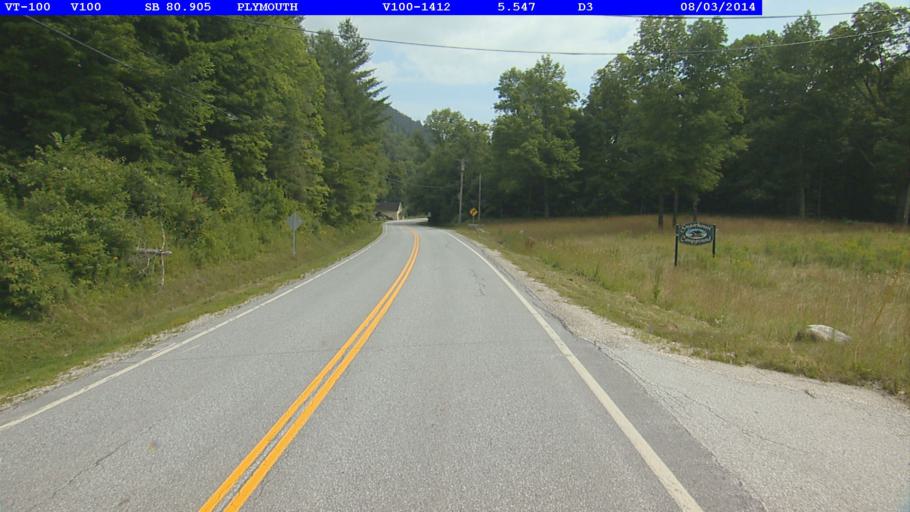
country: US
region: Vermont
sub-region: Windsor County
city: Woodstock
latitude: 43.5329
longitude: -72.7409
